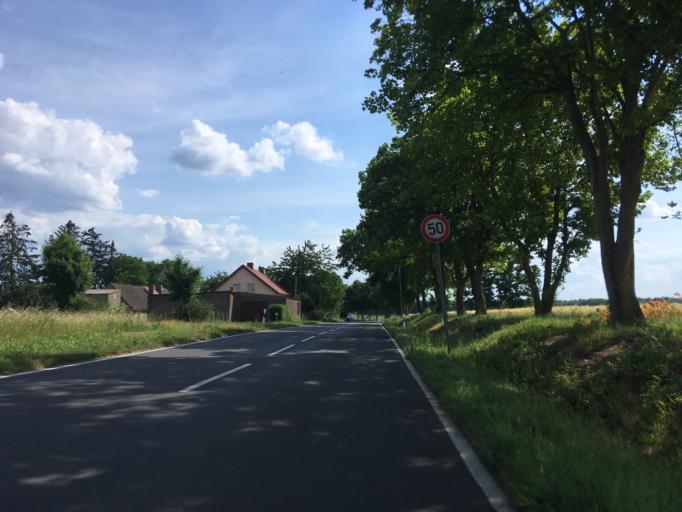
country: DE
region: Brandenburg
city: Steinhofel
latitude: 52.4389
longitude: 14.1009
